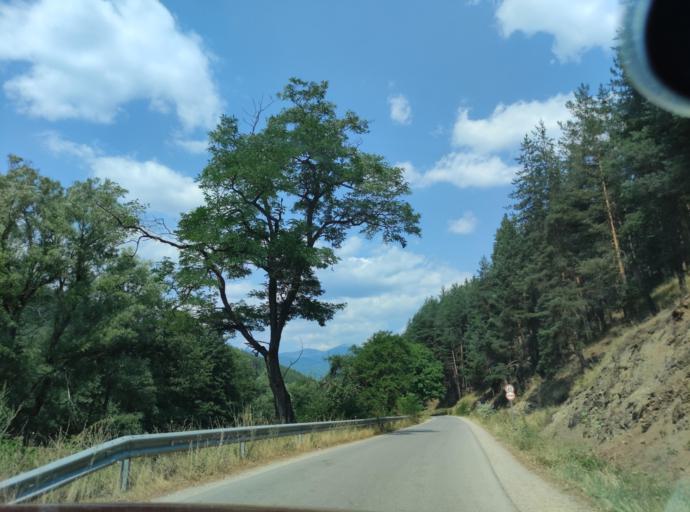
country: BG
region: Blagoevgrad
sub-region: Obshtina Belitsa
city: Belitsa
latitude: 41.9593
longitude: 23.5559
